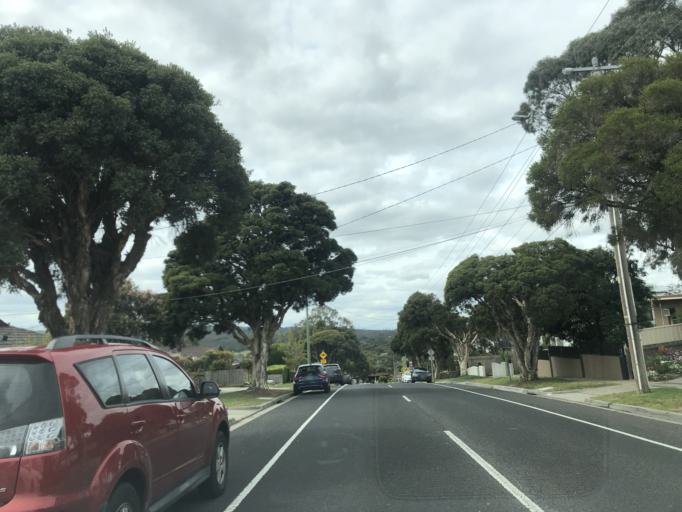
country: AU
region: Victoria
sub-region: Greater Dandenong
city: Dandenong North
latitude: -37.9500
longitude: 145.2187
